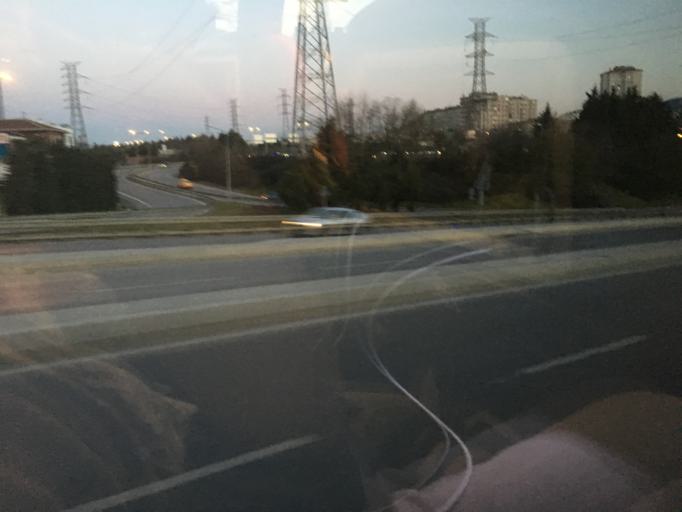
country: TR
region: Istanbul
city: Umraniye
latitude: 40.9959
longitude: 29.1551
